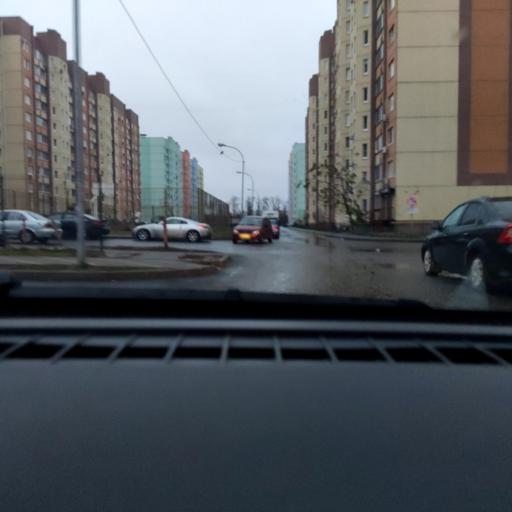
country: RU
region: Voronezj
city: Voronezh
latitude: 51.7143
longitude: 39.1868
